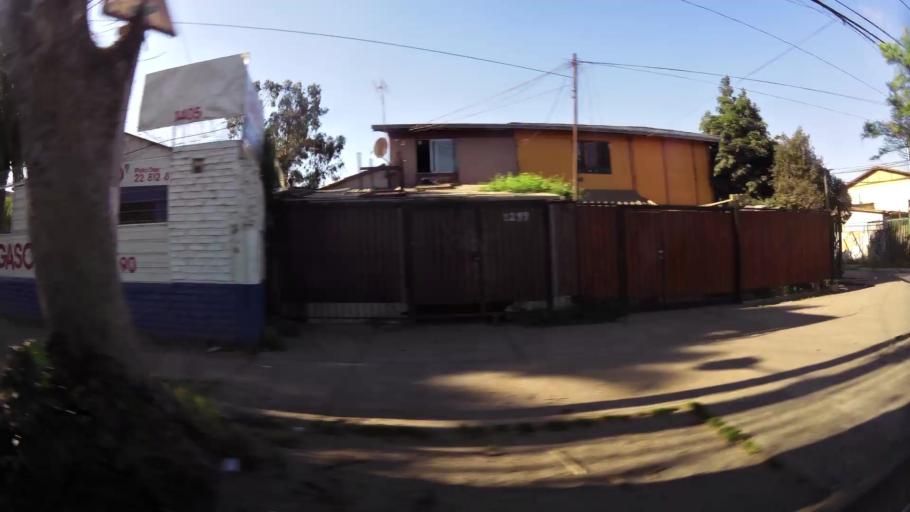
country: CL
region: Santiago Metropolitan
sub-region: Provincia de Talagante
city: Penaflor
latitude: -33.6051
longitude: -70.8681
